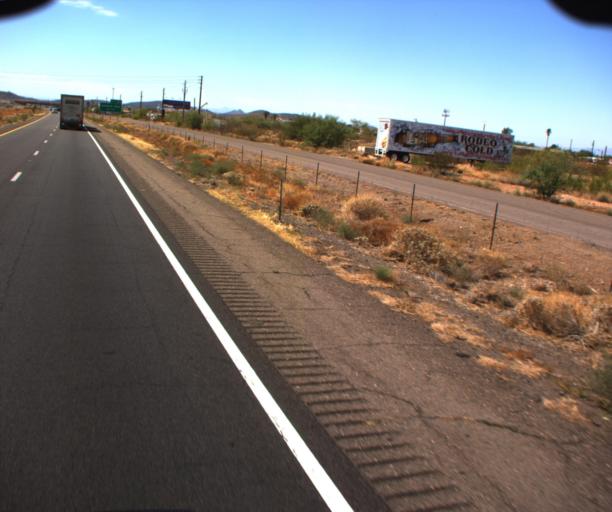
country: US
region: Arizona
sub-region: Maricopa County
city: Anthem
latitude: 33.8835
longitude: -112.1477
